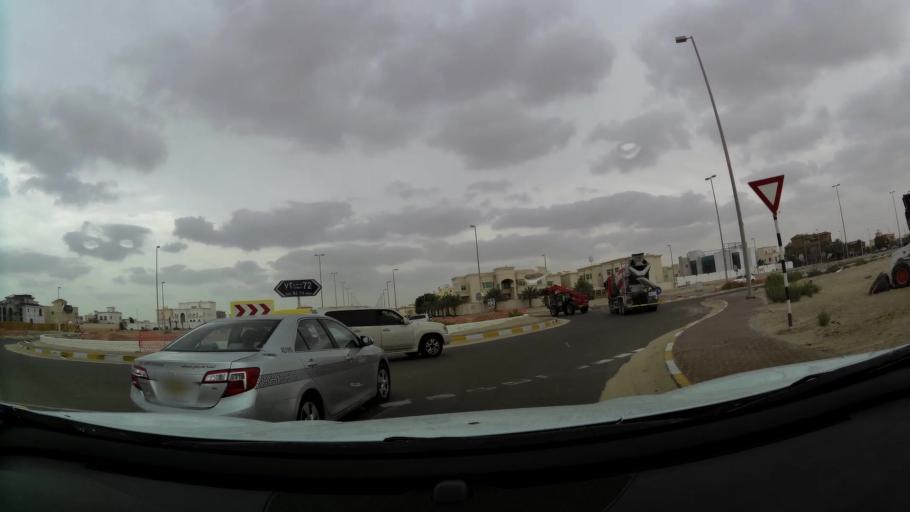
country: AE
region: Abu Dhabi
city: Abu Dhabi
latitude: 24.3758
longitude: 54.6444
